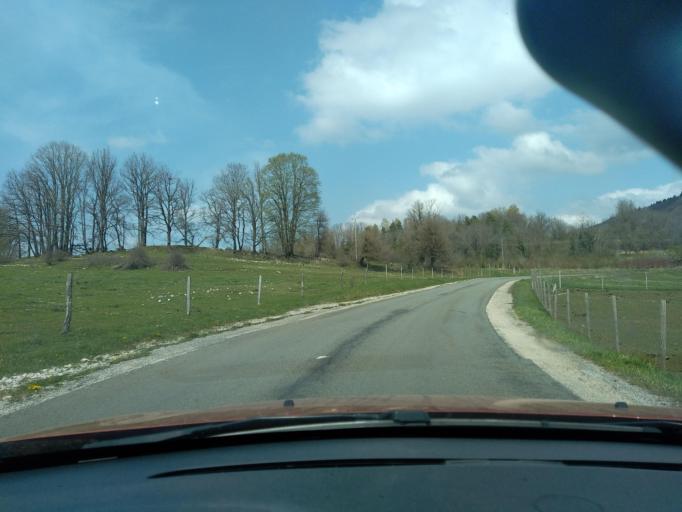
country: FR
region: Franche-Comte
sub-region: Departement du Jura
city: Moirans-en-Montagne
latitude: 46.4609
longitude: 5.7368
